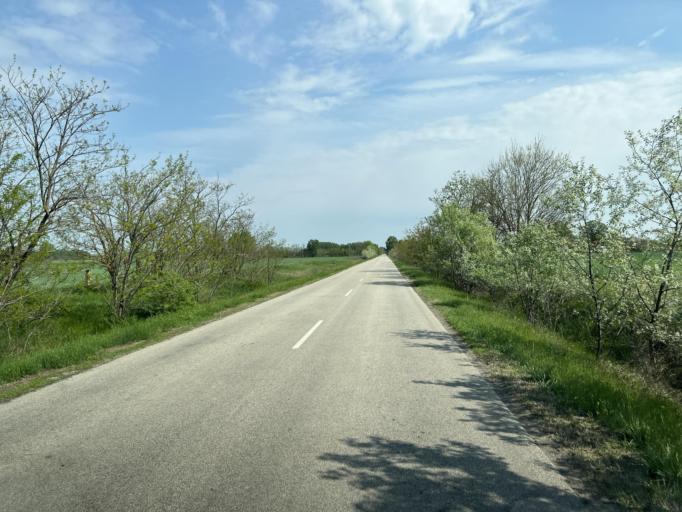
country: HU
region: Pest
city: Kocser
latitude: 47.0371
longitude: 19.9402
